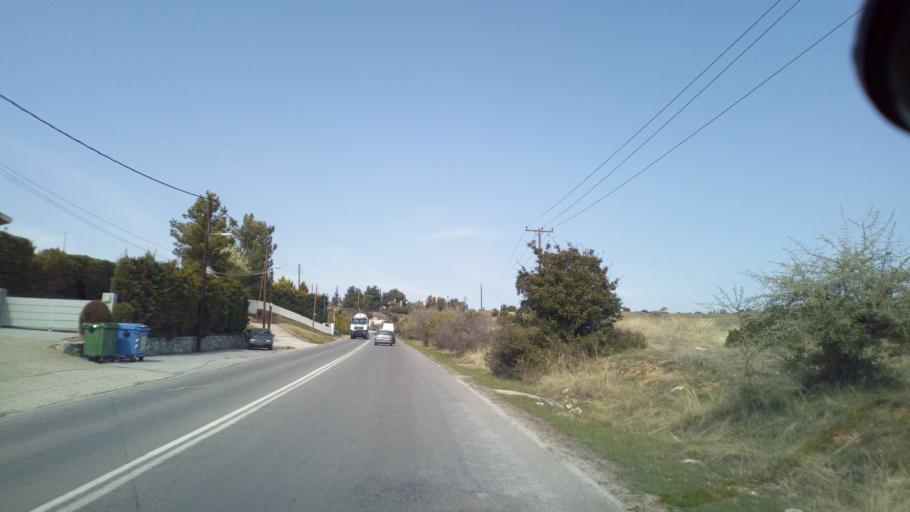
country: GR
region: Central Macedonia
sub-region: Nomos Thessalonikis
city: Thermi
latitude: 40.5662
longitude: 23.0251
